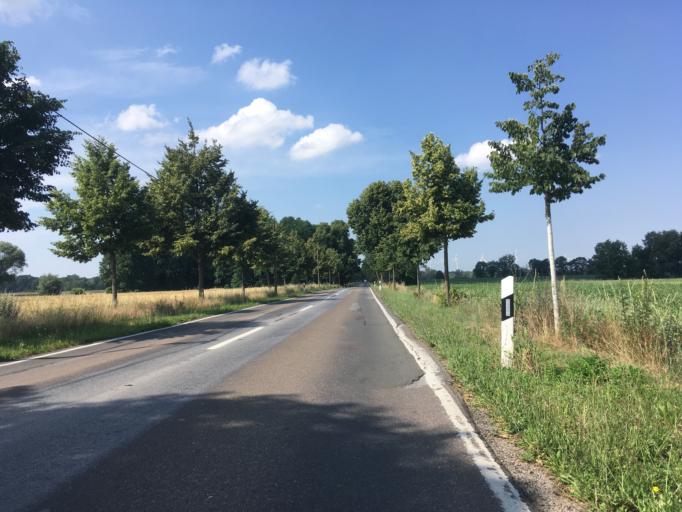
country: DE
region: Saxony-Anhalt
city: Quellendorf
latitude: 51.7932
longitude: 12.1683
